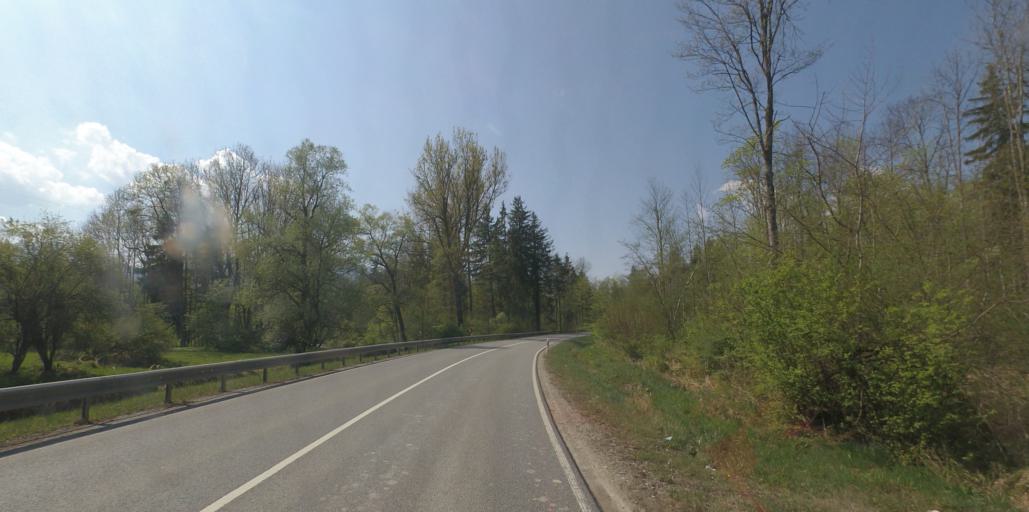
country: DE
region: Bavaria
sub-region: Upper Bavaria
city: Ubersee
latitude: 47.8215
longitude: 12.5108
